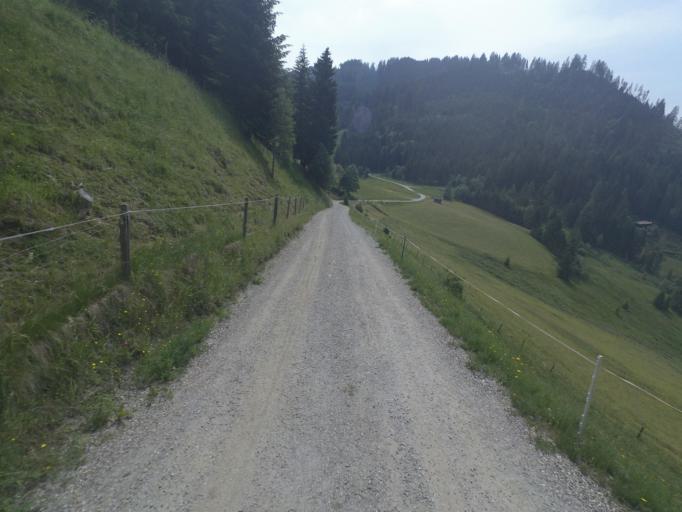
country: AT
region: Salzburg
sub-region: Politischer Bezirk Sankt Johann im Pongau
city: Muhlbach am Hochkonig
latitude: 47.3570
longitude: 13.1155
